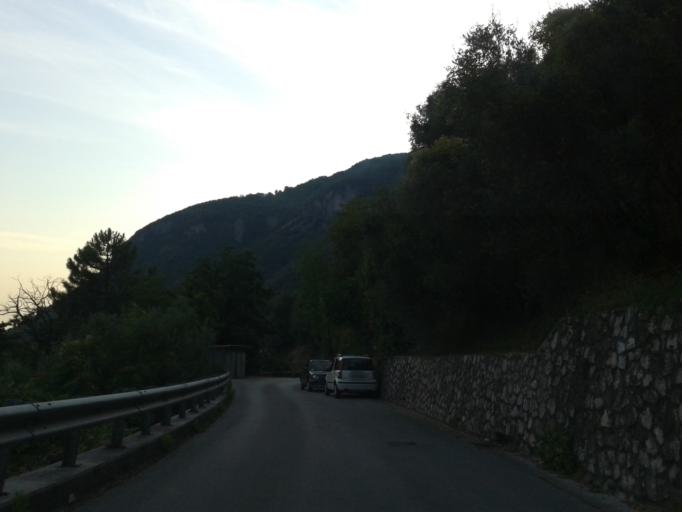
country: IT
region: Tuscany
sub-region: Provincia di Lucca
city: Pontestazzemese
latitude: 43.9604
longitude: 10.3260
